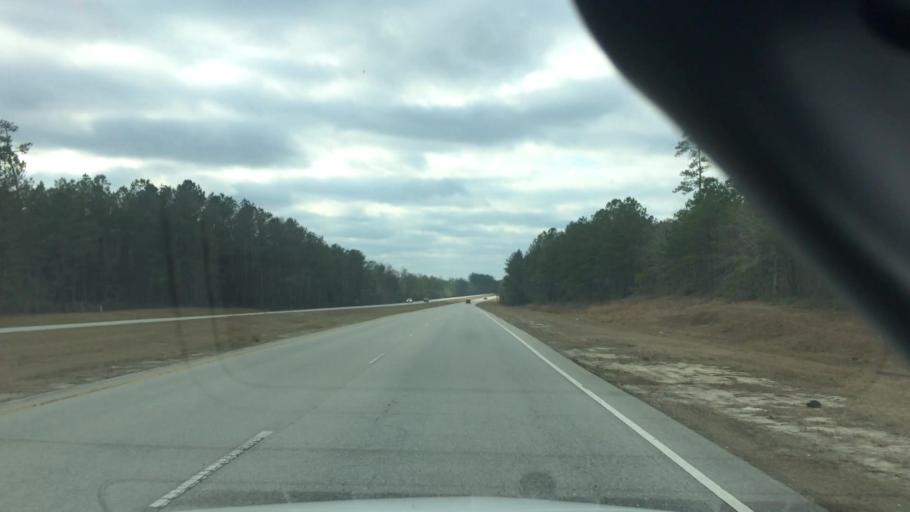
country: US
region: North Carolina
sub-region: Brunswick County
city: Bolivia
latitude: 34.0687
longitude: -78.1771
